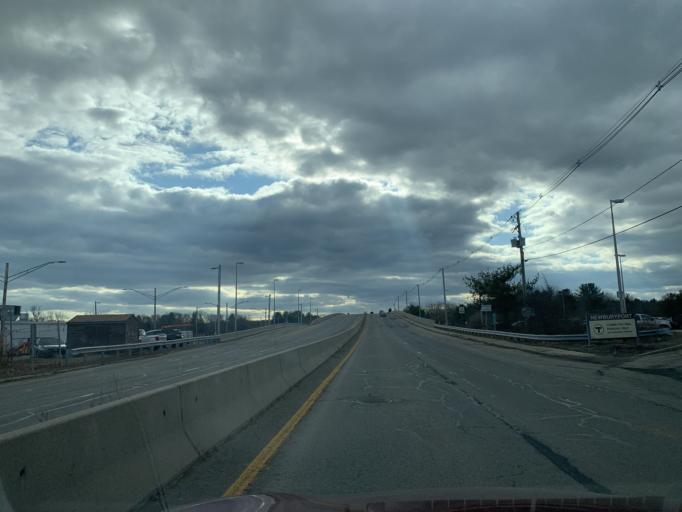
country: US
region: Massachusetts
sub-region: Essex County
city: Newburyport
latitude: 42.7972
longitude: -70.8759
